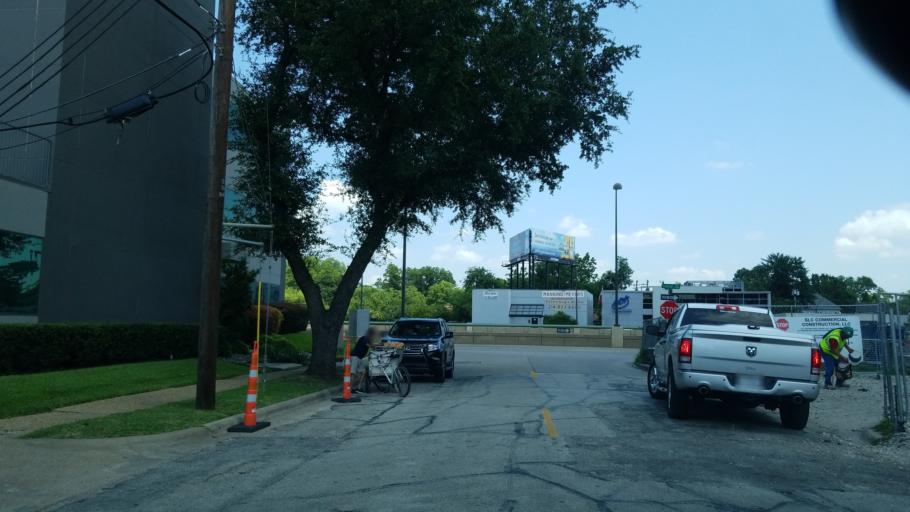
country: US
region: Texas
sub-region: Dallas County
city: Highland Park
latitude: 32.8191
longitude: -96.7884
